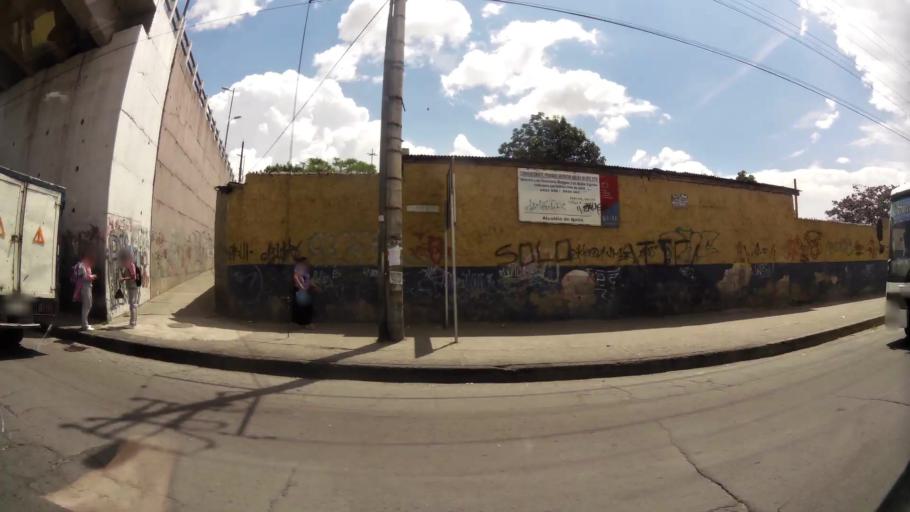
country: EC
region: Pichincha
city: Quito
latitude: -0.1043
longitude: -78.4226
